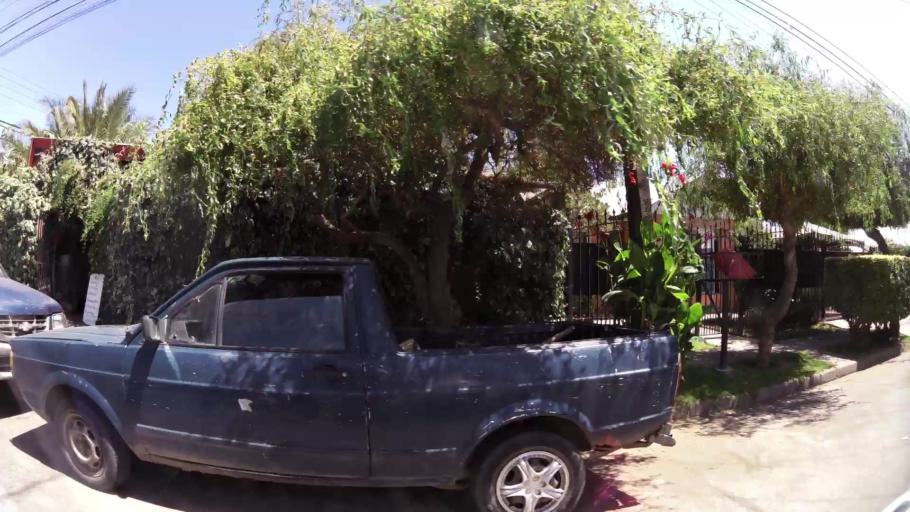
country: CL
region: Maule
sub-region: Provincia de Talca
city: Talca
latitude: -35.4295
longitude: -71.6293
